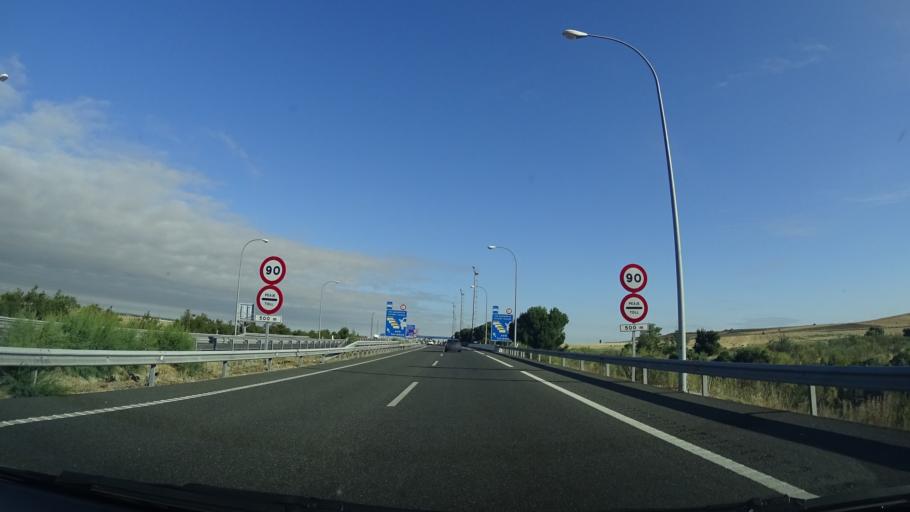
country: ES
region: Castille and Leon
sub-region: Provincia de Avila
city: Sanchidrian
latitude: 40.8794
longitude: -4.5687
